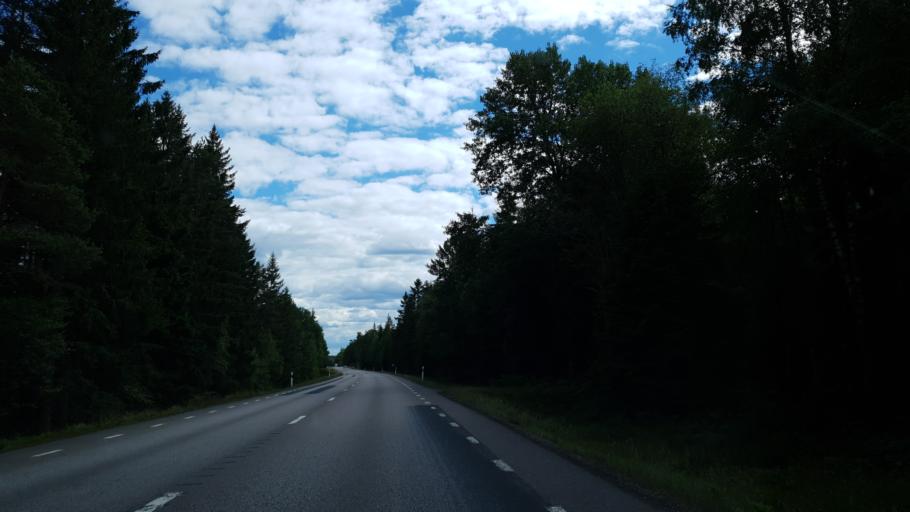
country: SE
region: Kronoberg
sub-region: Uppvidinge Kommun
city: Lenhovda
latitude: 56.8935
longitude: 15.3712
